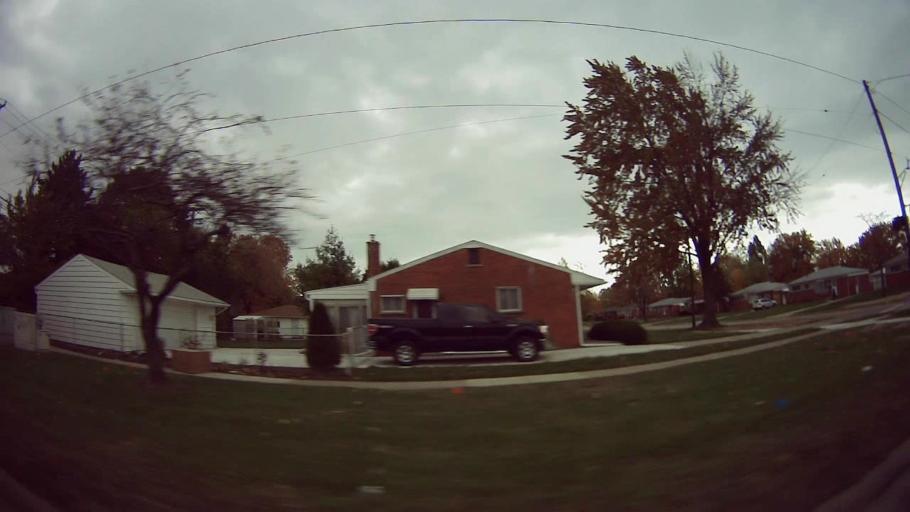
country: US
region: Michigan
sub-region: Macomb County
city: Center Line
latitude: 42.4838
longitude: -83.0062
